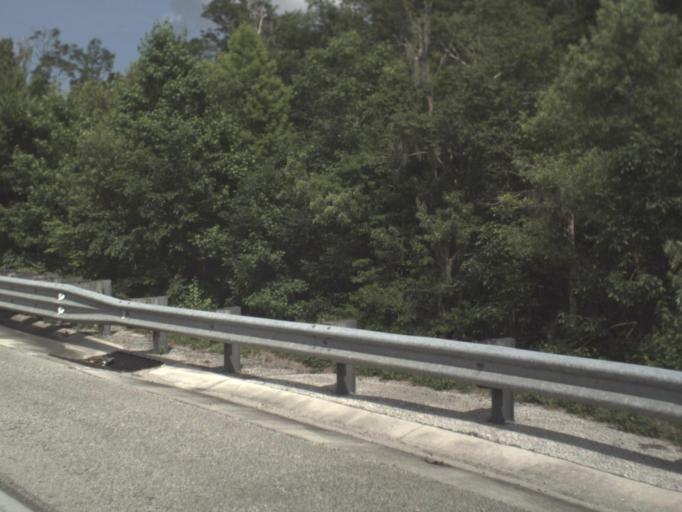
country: US
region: Florida
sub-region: Putnam County
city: East Palatka
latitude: 29.7226
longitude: -81.4857
